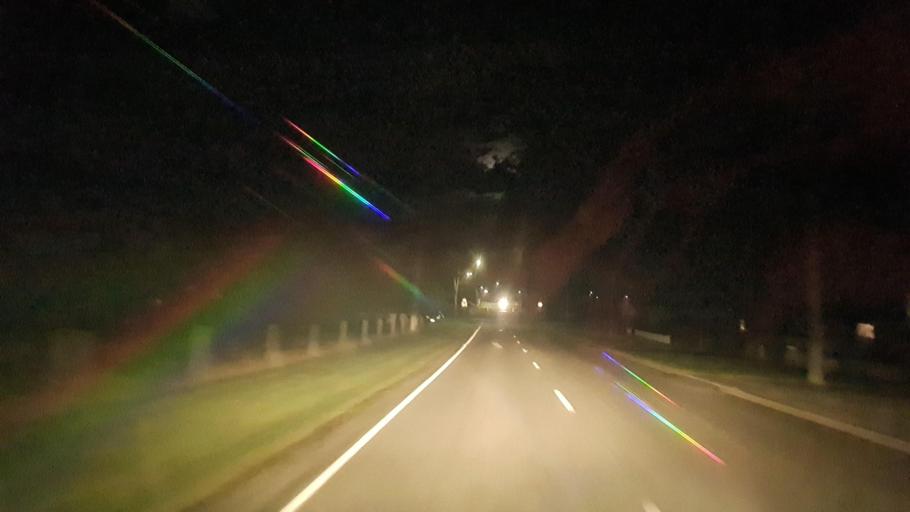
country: NZ
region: Otago
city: Oamaru
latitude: -45.0994
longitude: 170.9396
